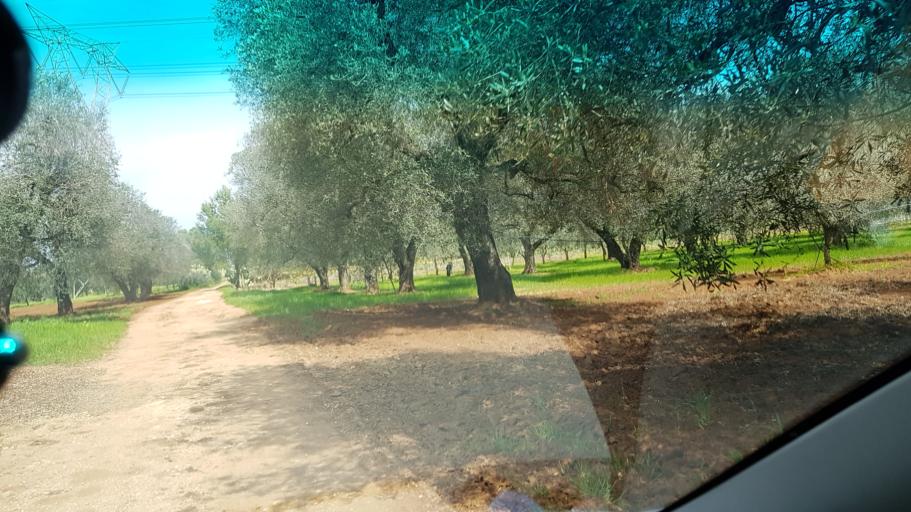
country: IT
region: Apulia
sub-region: Provincia di Brindisi
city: Mesagne
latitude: 40.6051
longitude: 17.8534
